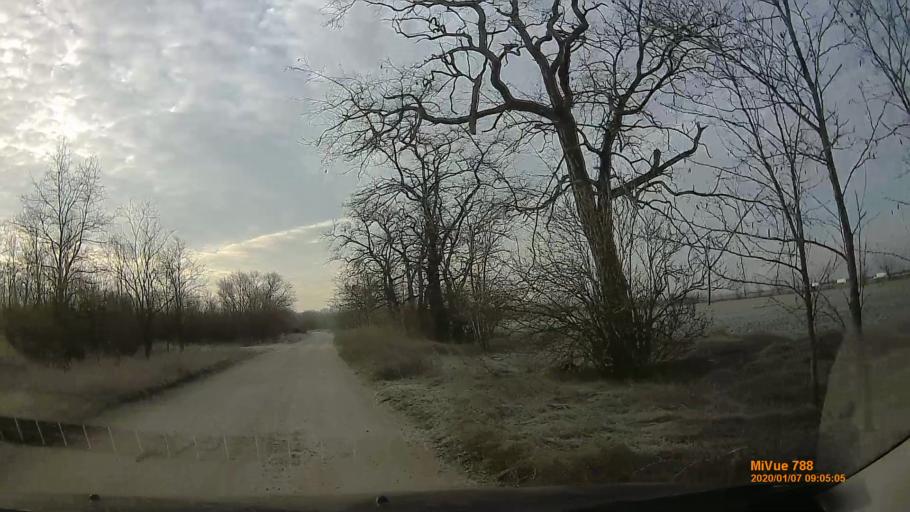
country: HU
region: Gyor-Moson-Sopron
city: Rajka
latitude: 47.9824
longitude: 17.1893
